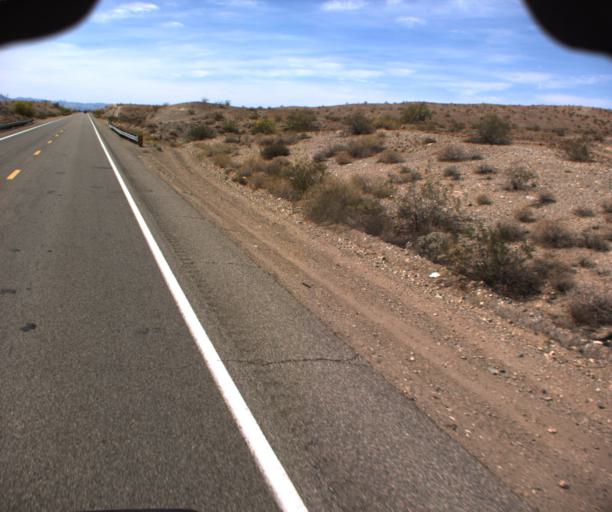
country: US
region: Arizona
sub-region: Mohave County
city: Lake Havasu City
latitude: 34.4391
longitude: -114.2272
